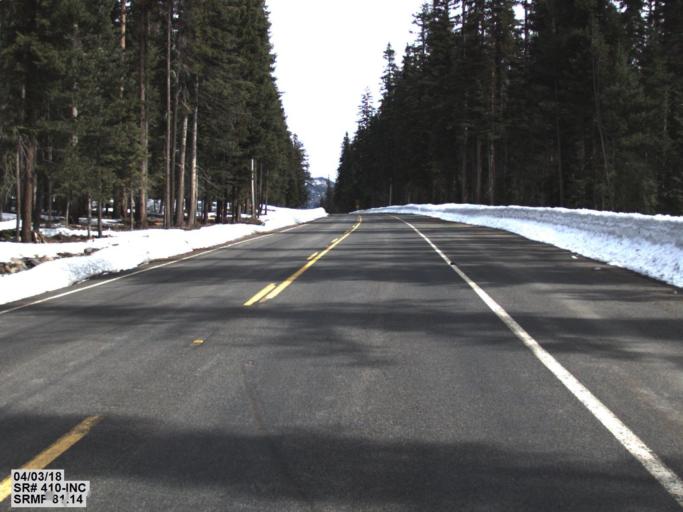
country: US
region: Washington
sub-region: Kittitas County
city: Cle Elum
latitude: 46.9502
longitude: -121.3115
